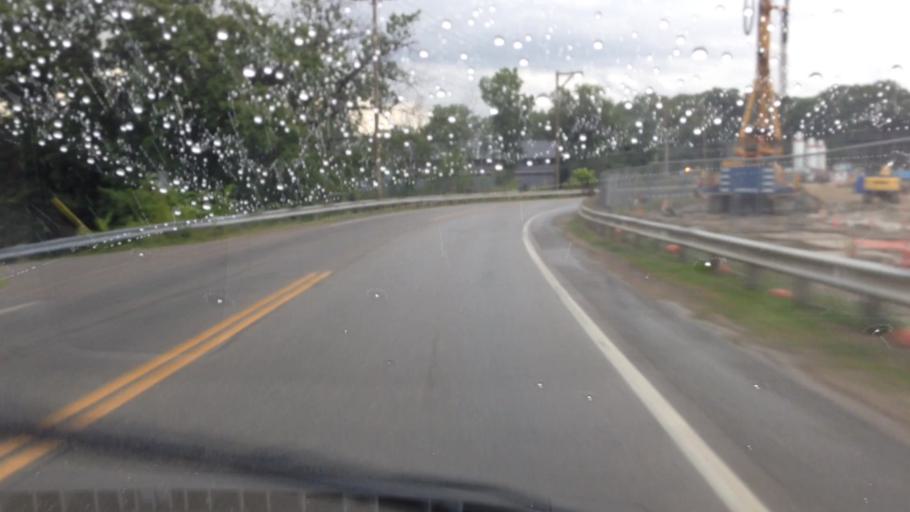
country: US
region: Ohio
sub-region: Summit County
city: Portage Lakes
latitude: 40.9985
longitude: -81.5331
